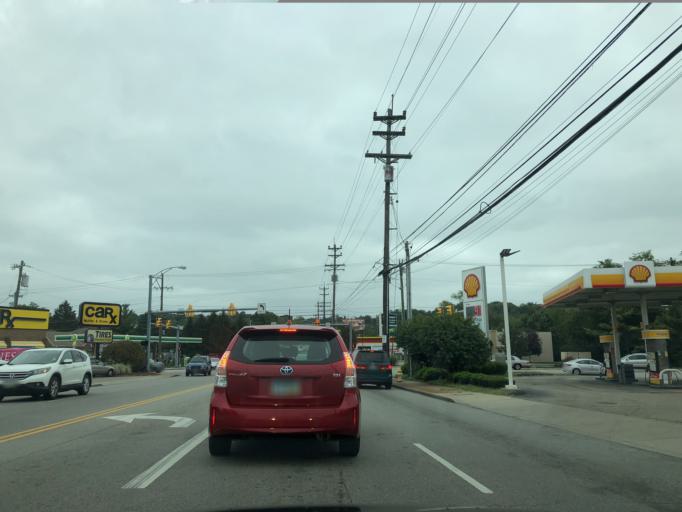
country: US
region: Ohio
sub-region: Hamilton County
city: Reading
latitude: 39.2116
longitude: -84.4486
